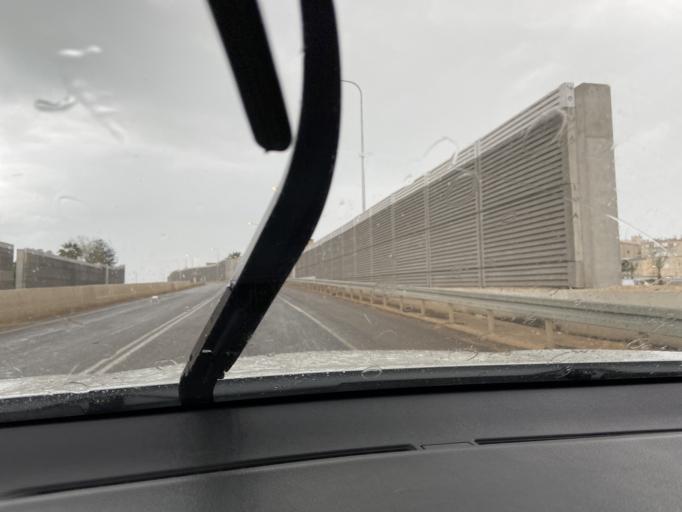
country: IL
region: Northern District
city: El Mazra`a
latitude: 32.9806
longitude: 35.1004
